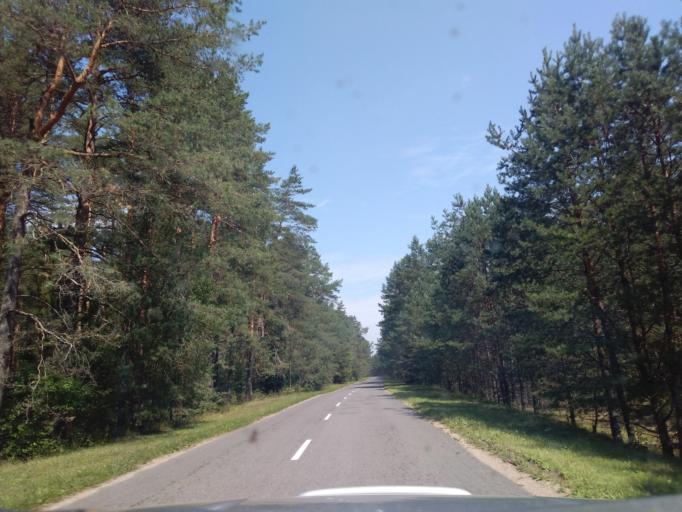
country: BY
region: Minsk
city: Valozhyn
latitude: 54.0234
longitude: 26.6036
